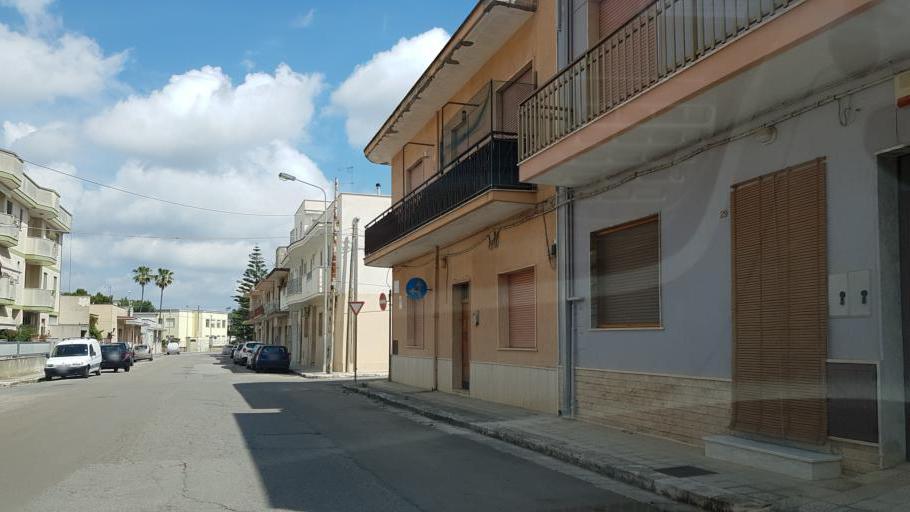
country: IT
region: Apulia
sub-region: Provincia di Brindisi
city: Mesagne
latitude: 40.5553
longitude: 17.8167
